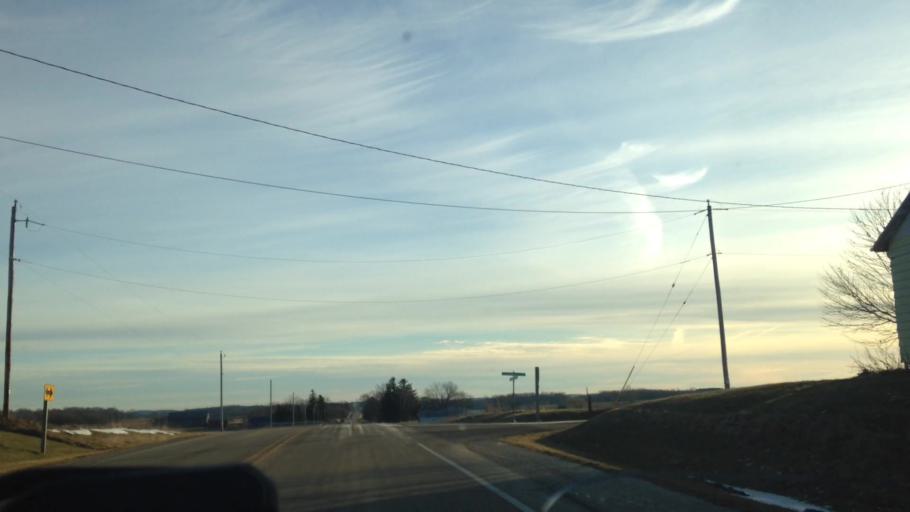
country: US
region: Wisconsin
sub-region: Dodge County
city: Theresa
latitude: 43.5365
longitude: -88.4904
